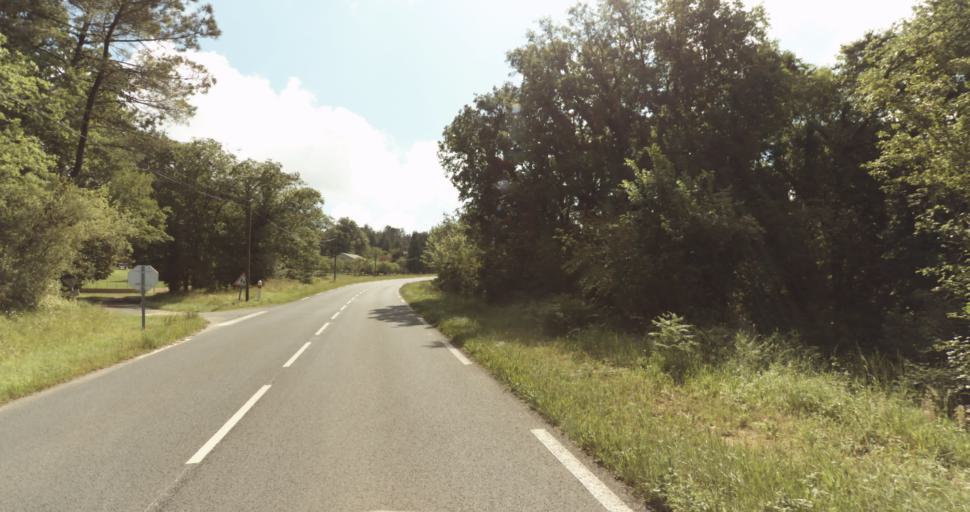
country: FR
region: Aquitaine
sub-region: Departement de la Dordogne
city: Le Bugue
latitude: 44.8398
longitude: 0.8623
